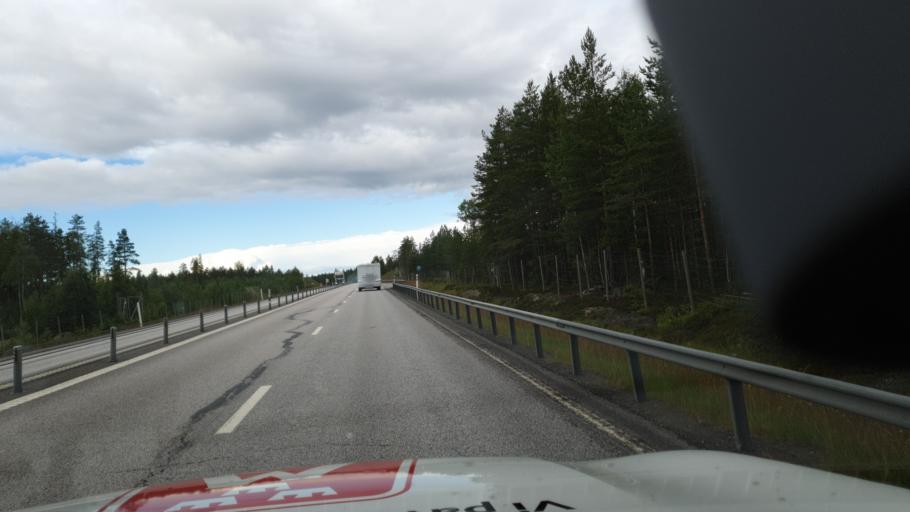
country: SE
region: Vaesterbotten
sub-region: Robertsfors Kommun
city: Robertsfors
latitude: 63.9905
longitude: 20.7559
